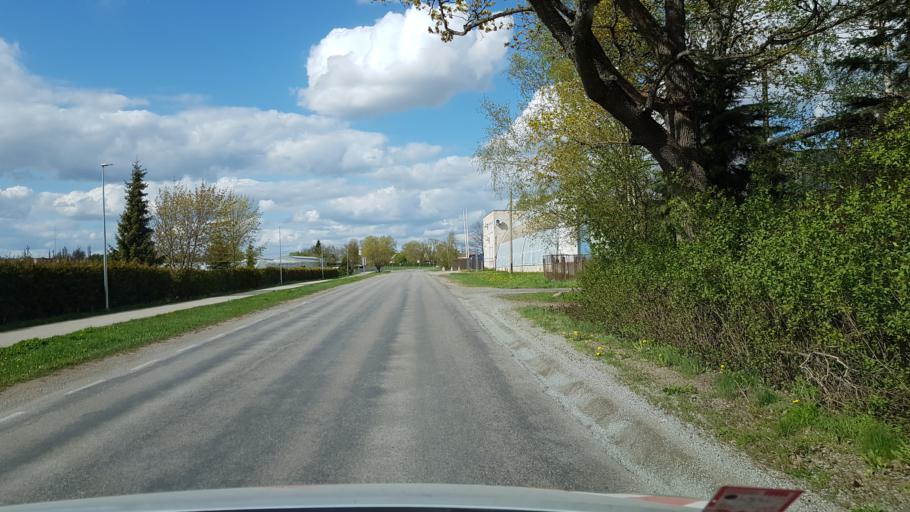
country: EE
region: Tartu
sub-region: Tartu linn
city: Tartu
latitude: 58.3665
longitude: 26.7987
